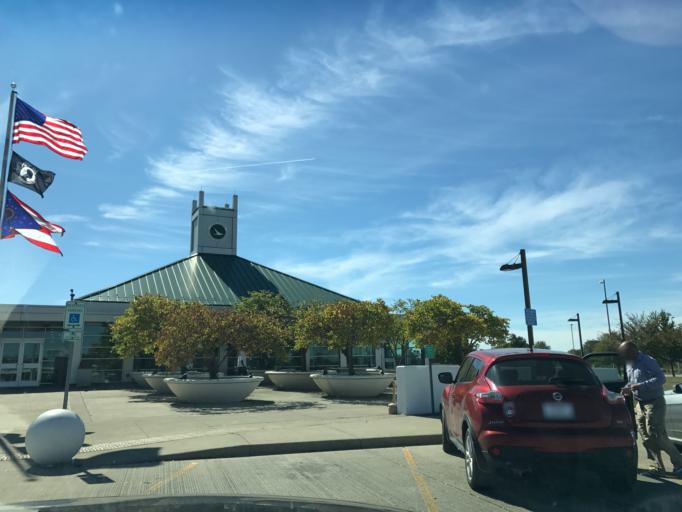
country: US
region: Ohio
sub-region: Licking County
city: Harbor Hills
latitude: 39.9462
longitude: -82.4526
